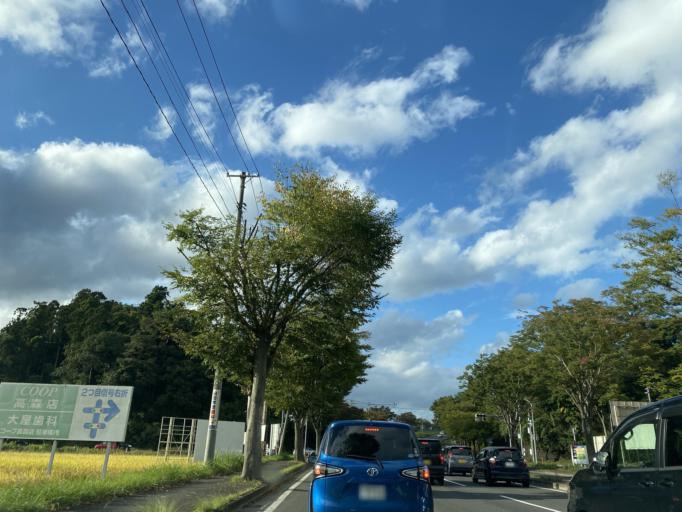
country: JP
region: Miyagi
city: Sendai-shi
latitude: 38.3282
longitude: 140.8417
